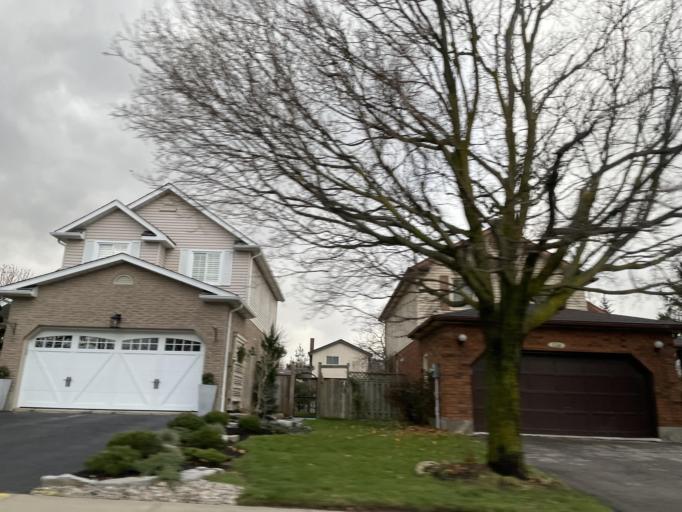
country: CA
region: Ontario
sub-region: Wellington County
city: Guelph
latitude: 43.5330
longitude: -80.2945
